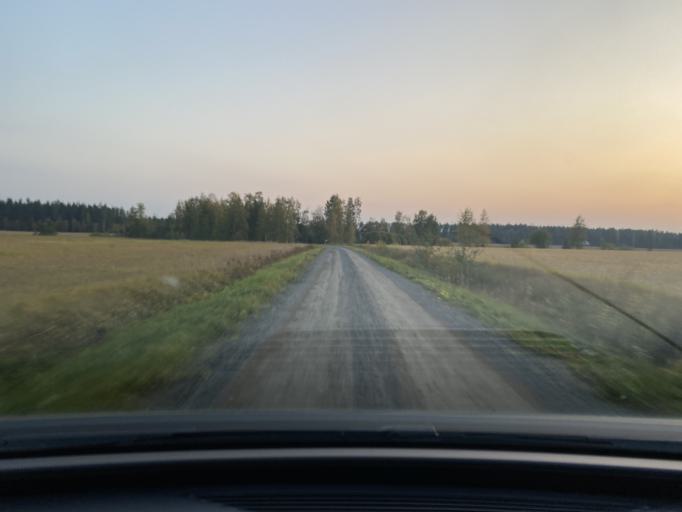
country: FI
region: Pirkanmaa
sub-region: Lounais-Pirkanmaa
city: Punkalaidun
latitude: 61.1149
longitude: 23.2416
